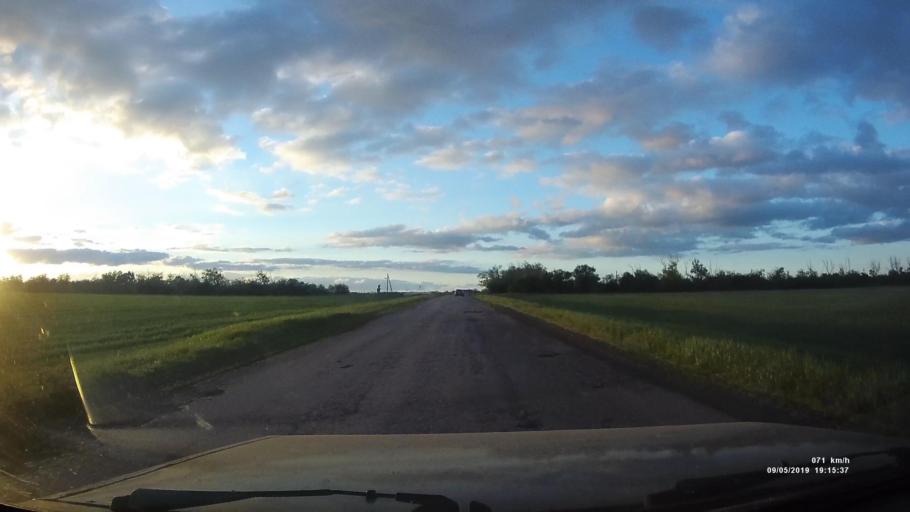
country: RU
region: Krasnodarskiy
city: Kanelovskaya
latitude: 46.7693
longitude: 39.2113
